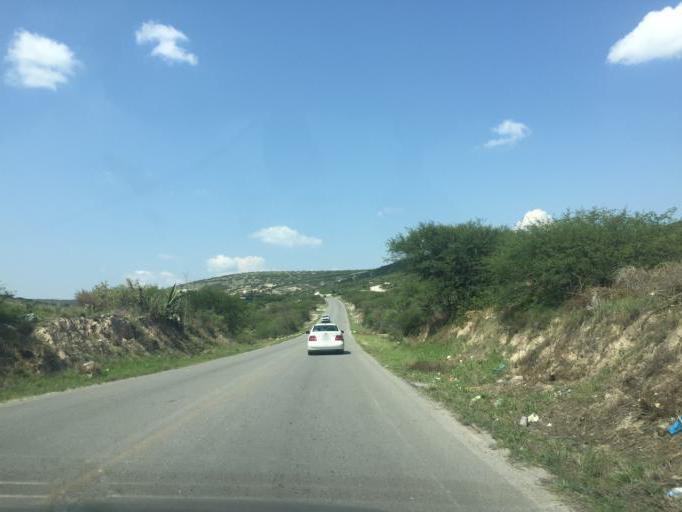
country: MX
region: Hidalgo
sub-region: Cardonal
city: Pozuelos
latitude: 20.5994
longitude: -99.1152
